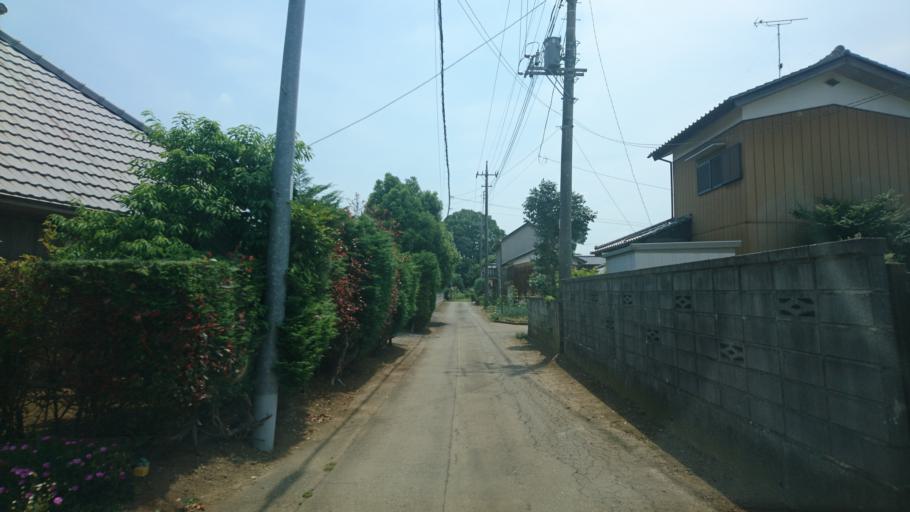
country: JP
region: Ibaraki
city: Mitsukaido
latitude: 36.0417
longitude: 139.9749
